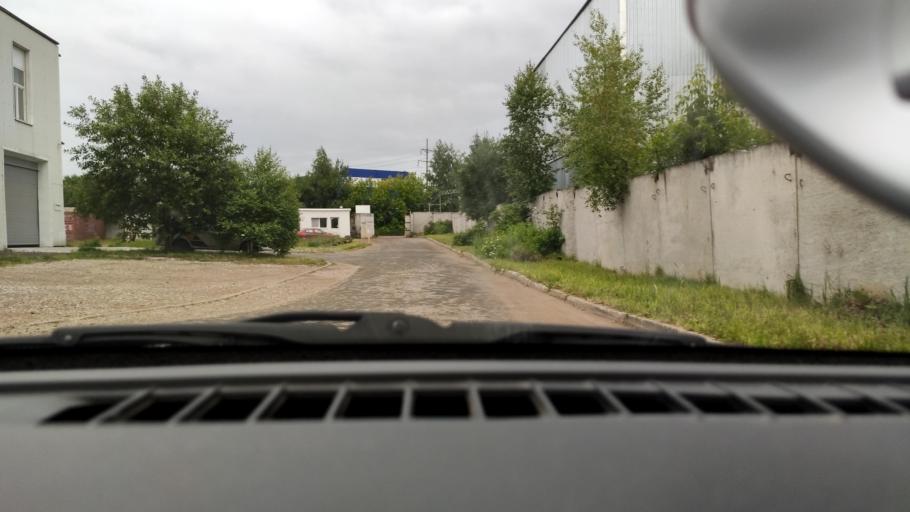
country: RU
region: Perm
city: Froly
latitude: 57.9718
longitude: 56.2890
